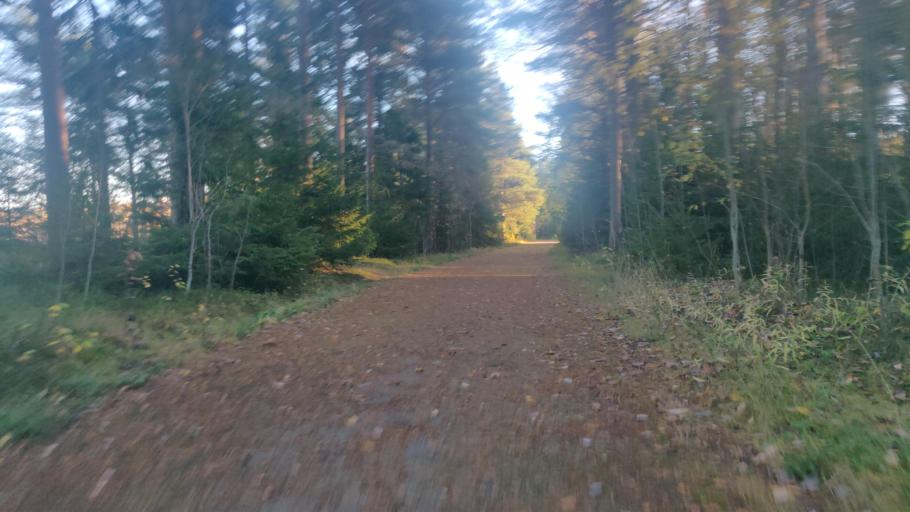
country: SE
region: Vaesternorrland
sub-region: Sundsvalls Kommun
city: Njurundabommen
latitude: 62.2699
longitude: 17.3978
